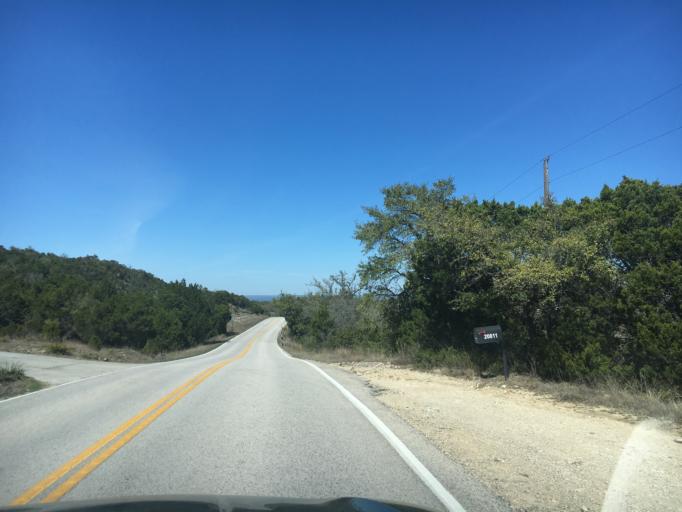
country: US
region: Texas
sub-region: Travis County
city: Briarcliff
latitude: 30.3065
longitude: -98.0893
